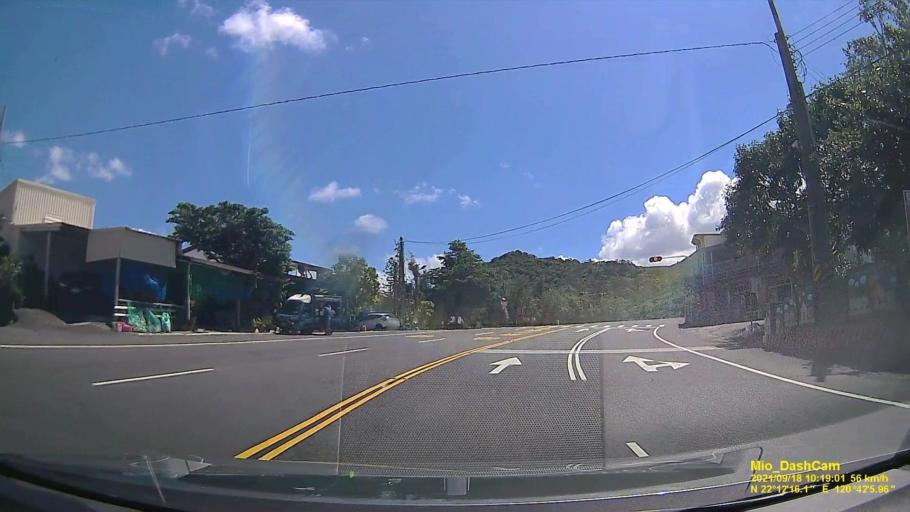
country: TW
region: Taiwan
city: Hengchun
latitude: 22.2045
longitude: 120.7017
